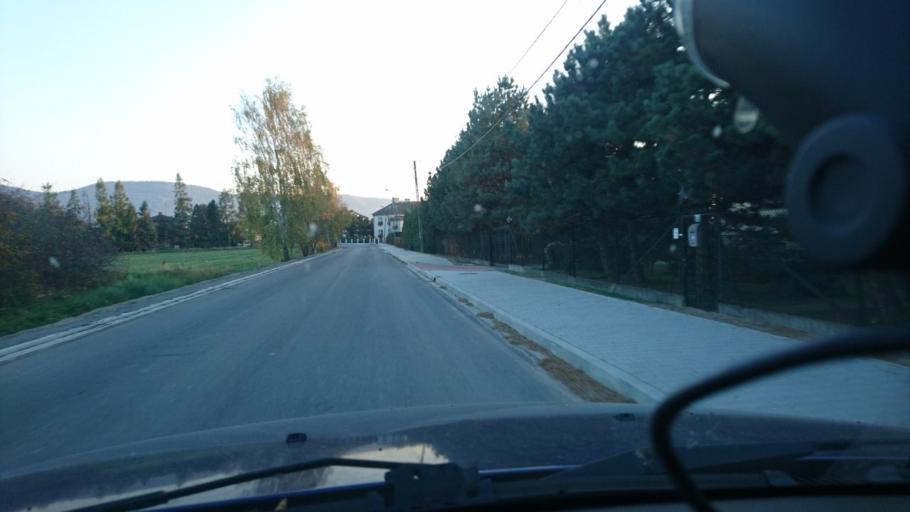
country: PL
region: Silesian Voivodeship
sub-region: Powiat bielski
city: Kozy
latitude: 49.8599
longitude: 19.1335
